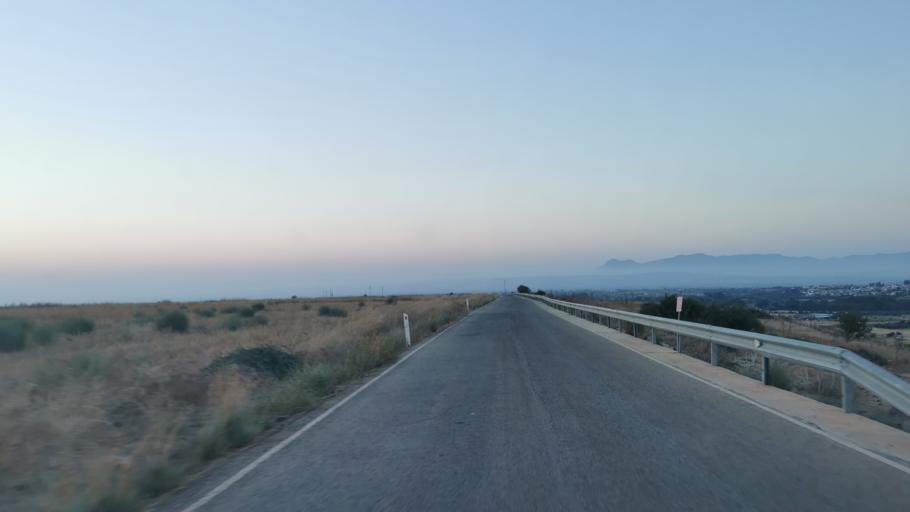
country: CY
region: Lefkosia
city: Peristerona
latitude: 35.0834
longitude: 33.0822
